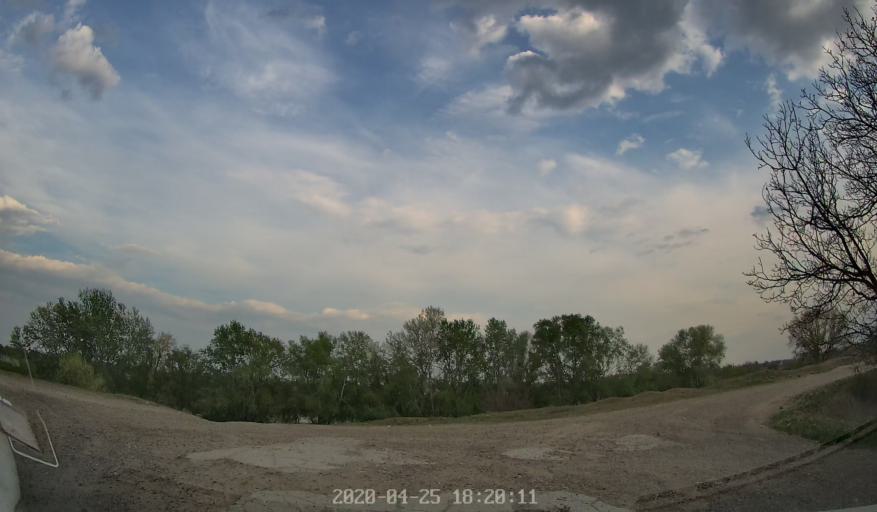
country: MD
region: Criuleni
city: Criuleni
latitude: 47.1573
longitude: 29.1330
